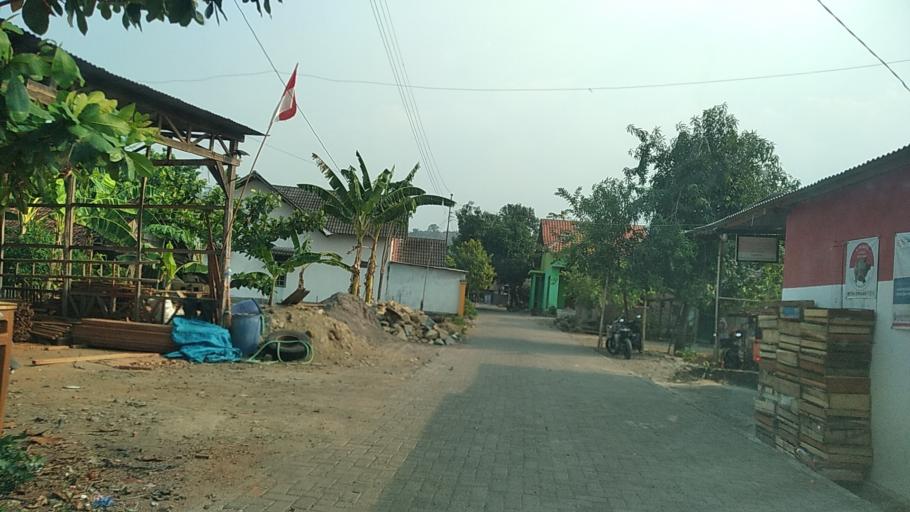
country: ID
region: Central Java
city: Mranggen
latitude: -7.0729
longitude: 110.4745
